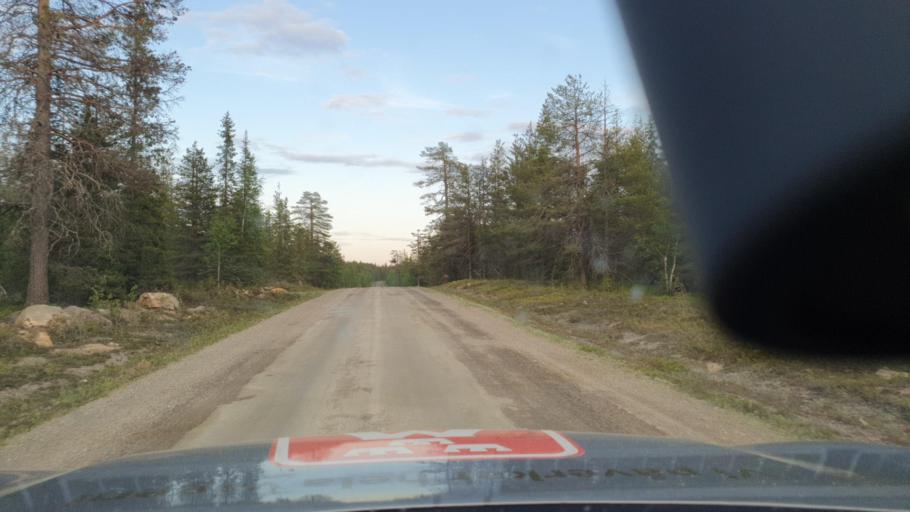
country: SE
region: Norrbotten
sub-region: Bodens Kommun
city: Boden
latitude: 66.5553
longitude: 21.4499
